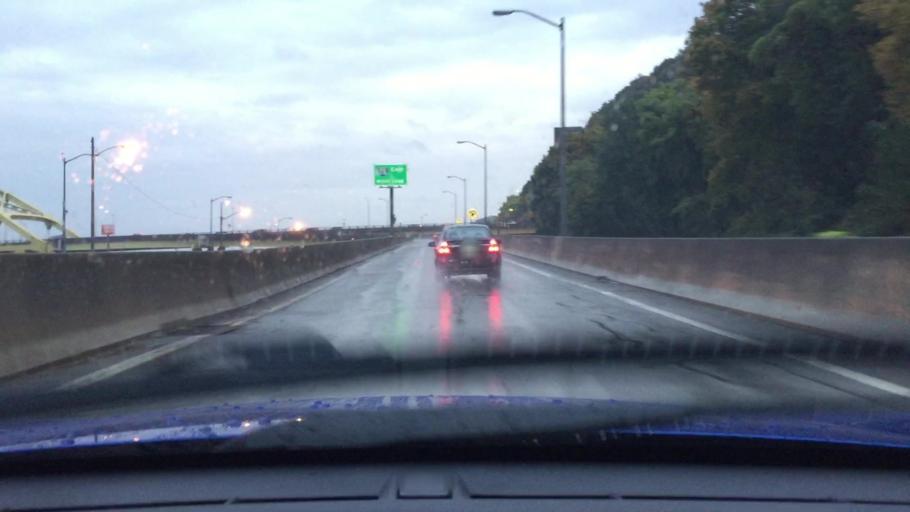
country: US
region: Pennsylvania
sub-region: Allegheny County
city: Pittsburgh
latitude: 40.4389
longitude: -80.0157
